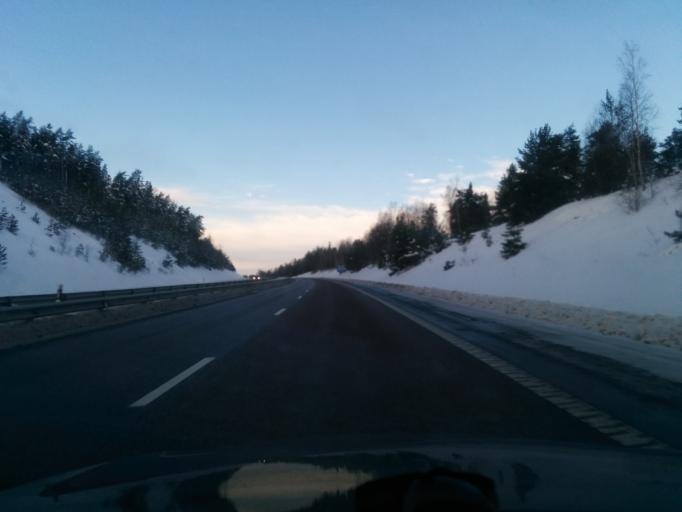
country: SE
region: Uppsala
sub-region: Habo Kommun
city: Balsta
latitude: 59.5761
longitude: 17.5416
